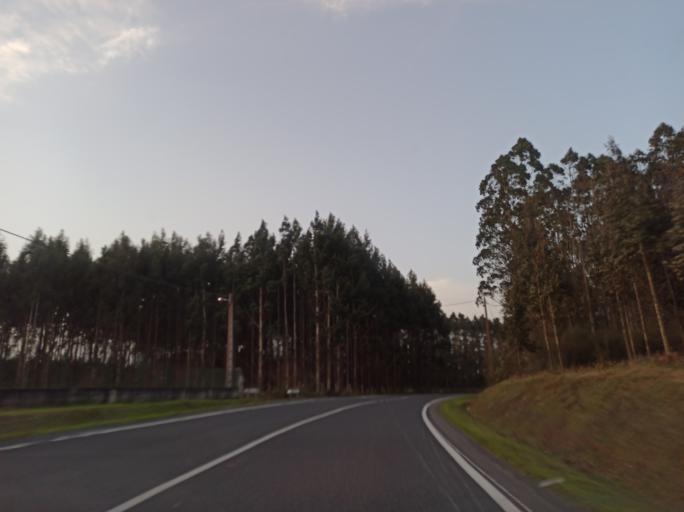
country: ES
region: Galicia
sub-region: Provincia da Coruna
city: Coiros
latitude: 43.1803
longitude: -8.1224
